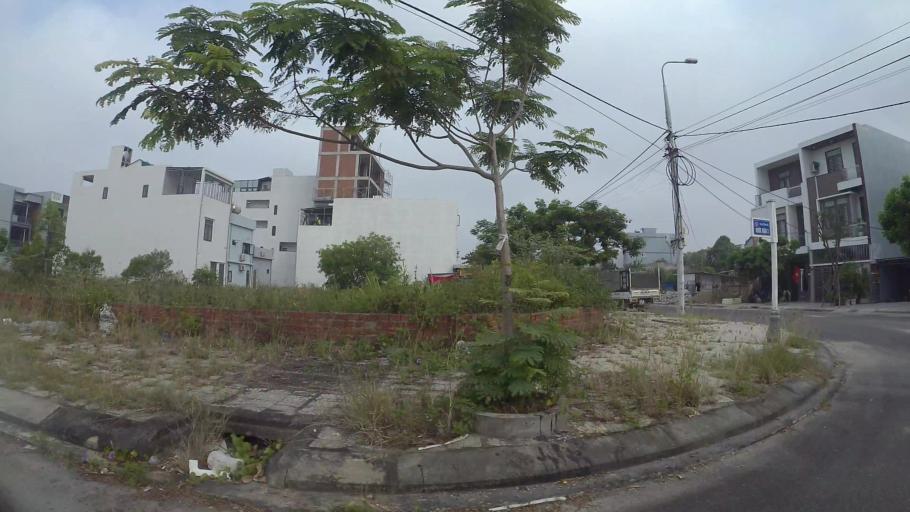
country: VN
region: Da Nang
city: Ngu Hanh Son
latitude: 16.0211
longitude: 108.2463
